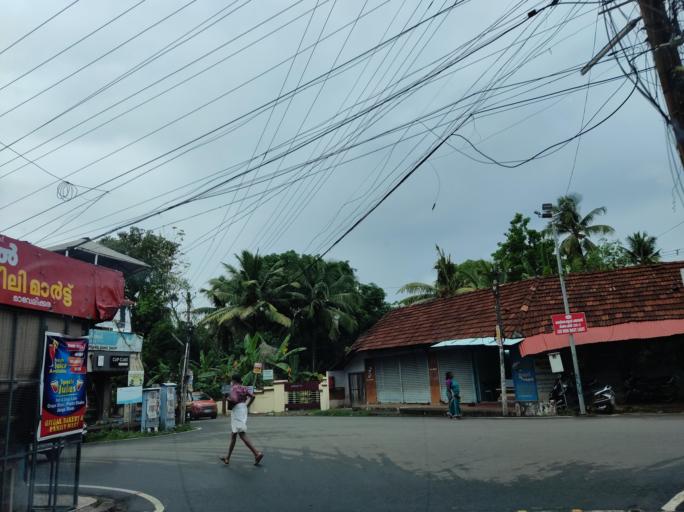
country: IN
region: Kerala
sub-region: Alappuzha
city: Mavelikara
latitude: 9.2408
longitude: 76.5534
